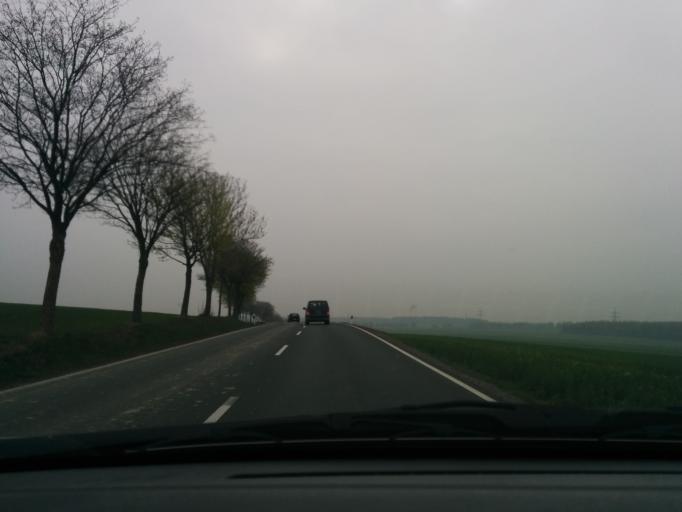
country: DE
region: Saxony
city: Oberschona
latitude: 50.9026
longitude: 13.2669
